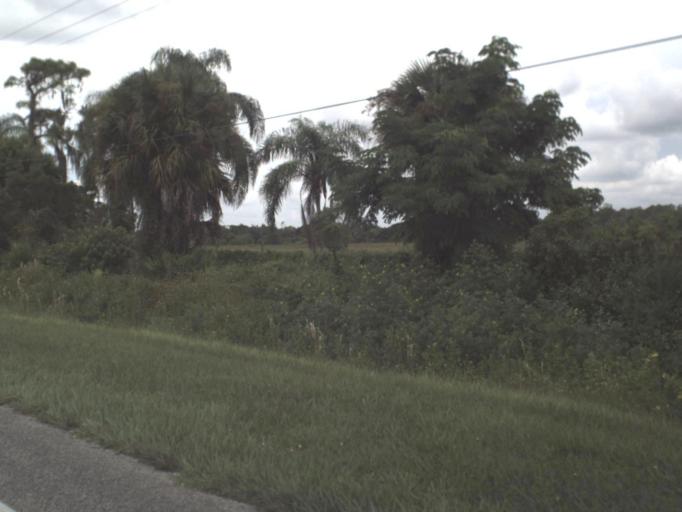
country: US
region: Florida
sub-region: Lee County
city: Olga
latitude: 26.7154
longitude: -81.6830
